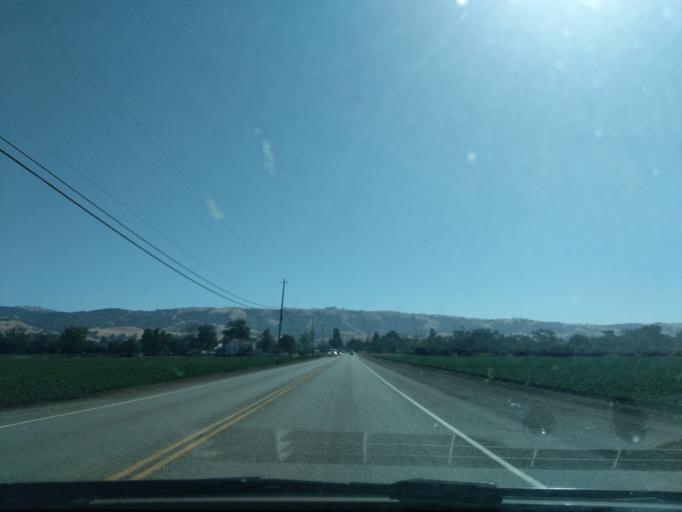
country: US
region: California
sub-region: Santa Clara County
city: Gilroy
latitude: 37.0298
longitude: -121.5476
